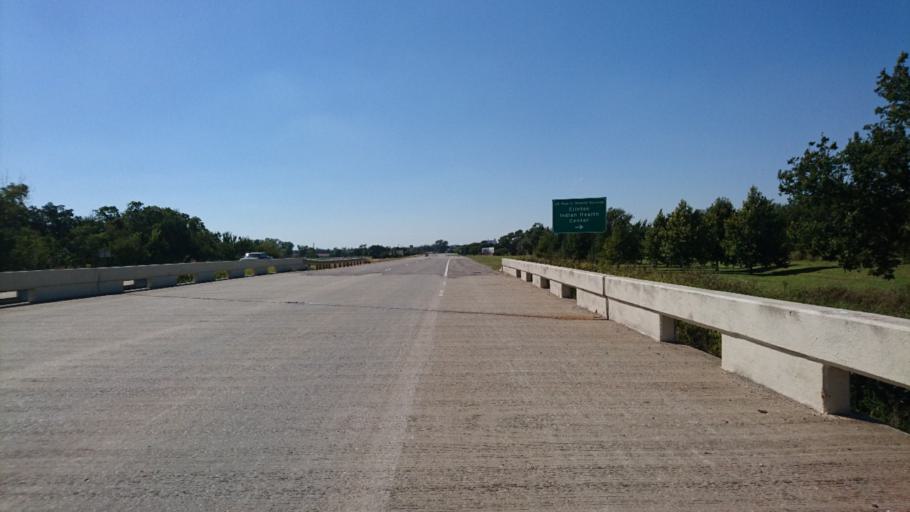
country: US
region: Oklahoma
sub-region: Custer County
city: Clinton
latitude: 35.5155
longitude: -98.9302
